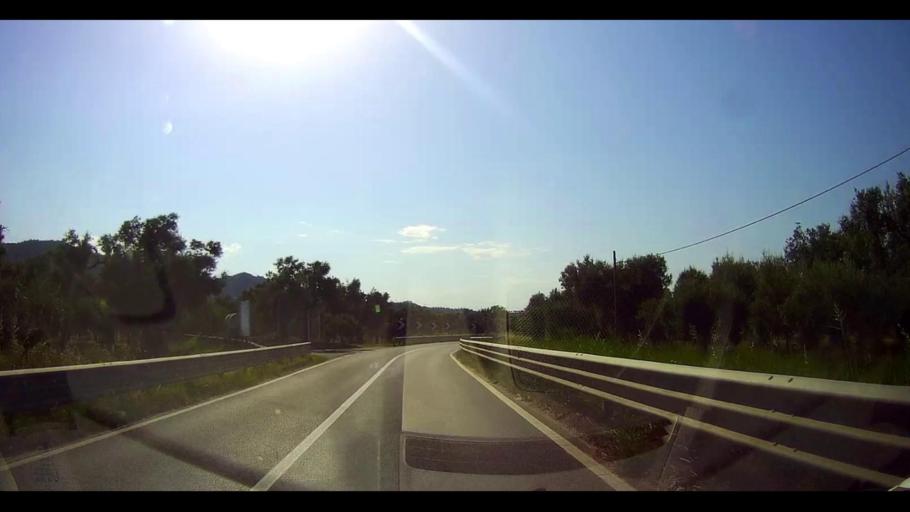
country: IT
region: Calabria
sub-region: Provincia di Cosenza
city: Cariati
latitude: 39.4820
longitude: 16.9788
